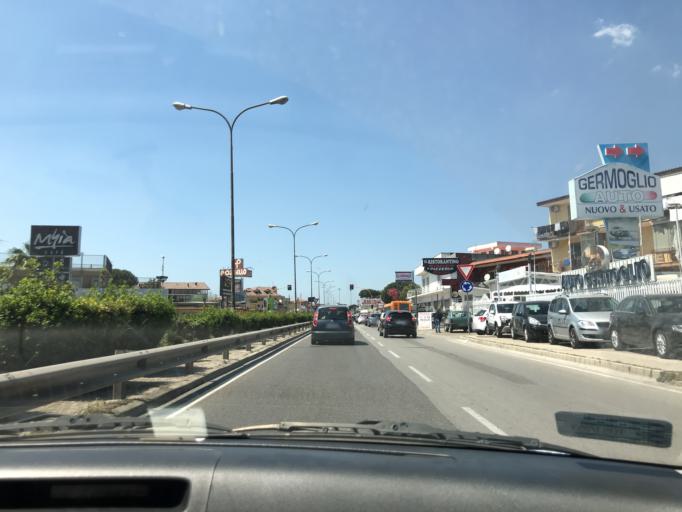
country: IT
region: Campania
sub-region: Provincia di Napoli
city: Villaricca
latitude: 40.9219
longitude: 14.1751
